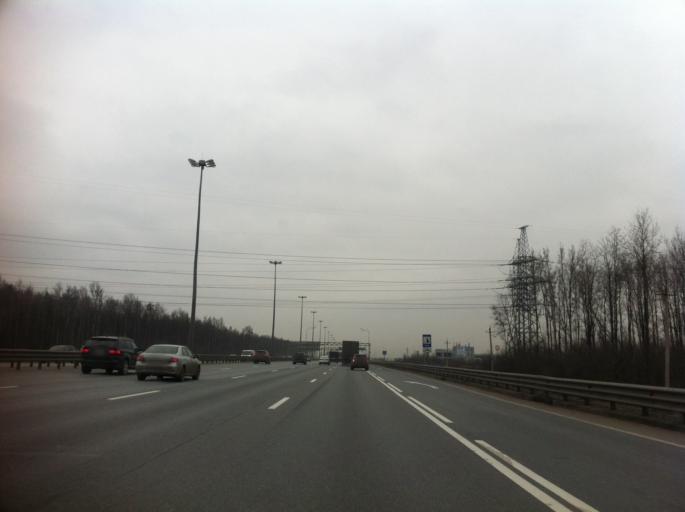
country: RU
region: Leningrad
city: Rybatskoye
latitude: 59.8846
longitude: 30.5256
